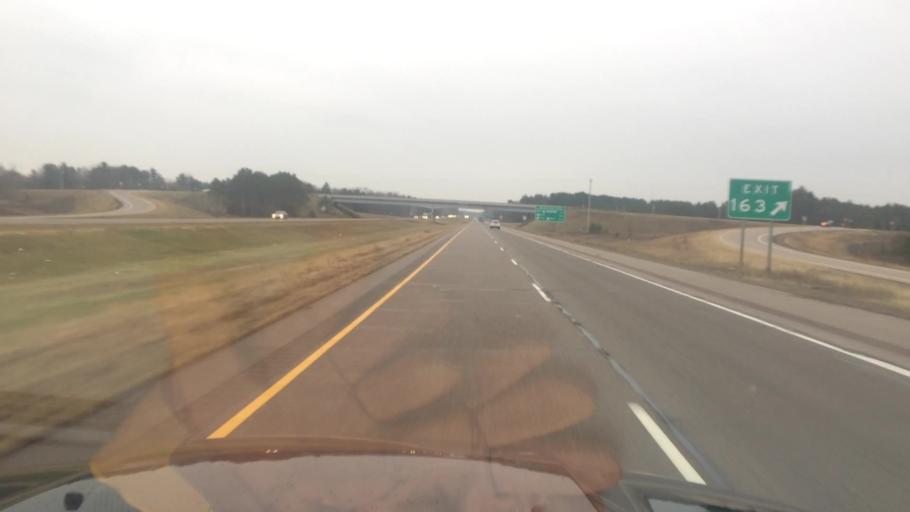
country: US
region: Wisconsin
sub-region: Portage County
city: Stevens Point
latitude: 44.5725
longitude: -89.6005
